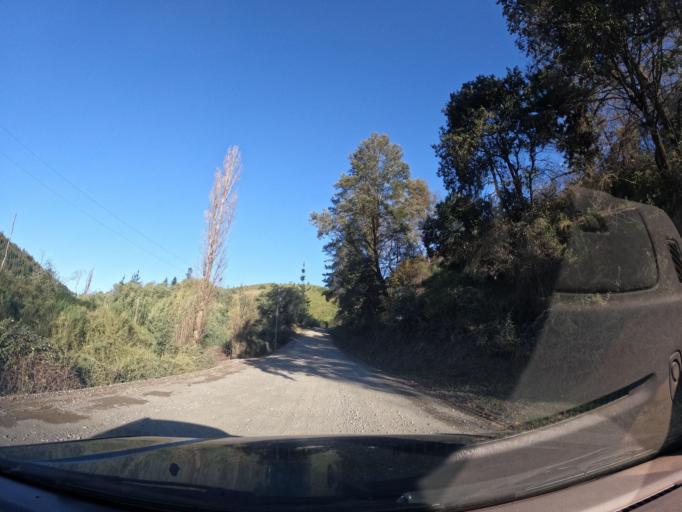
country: CL
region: Biobio
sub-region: Provincia de Concepcion
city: Chiguayante
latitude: -37.0140
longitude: -72.8928
